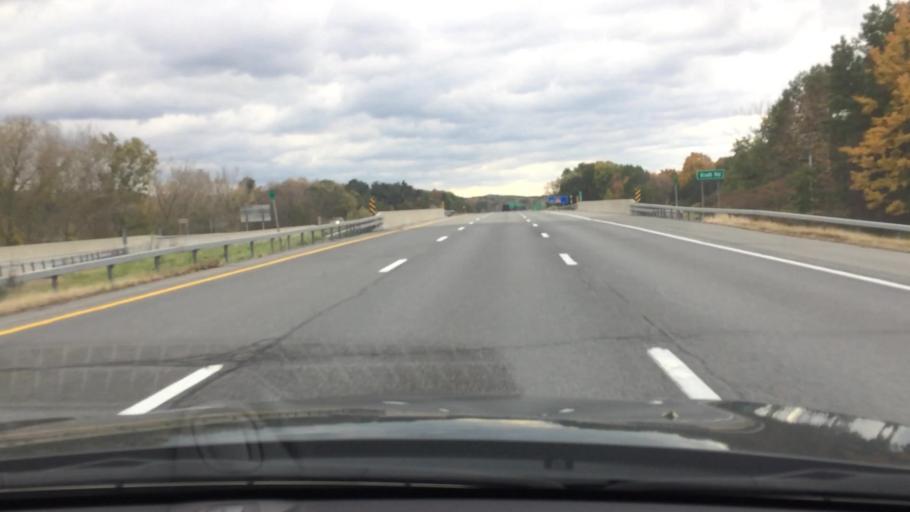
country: US
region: New York
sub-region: Rensselaer County
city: East Greenbush
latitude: 42.5694
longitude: -73.6791
